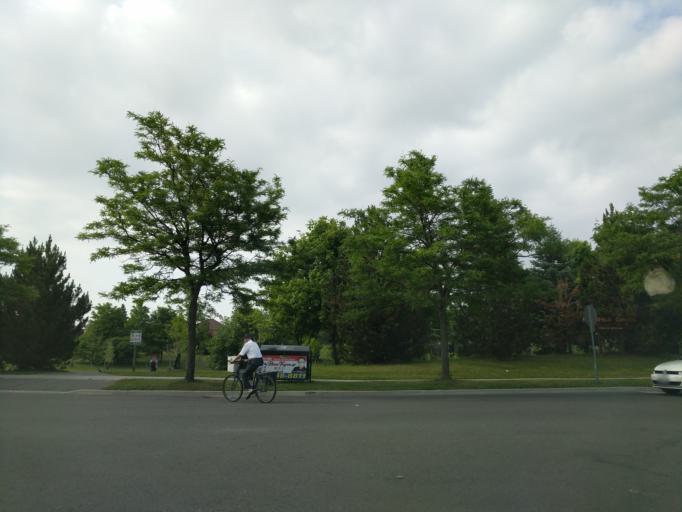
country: CA
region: Ontario
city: Markham
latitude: 43.8370
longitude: -79.2692
